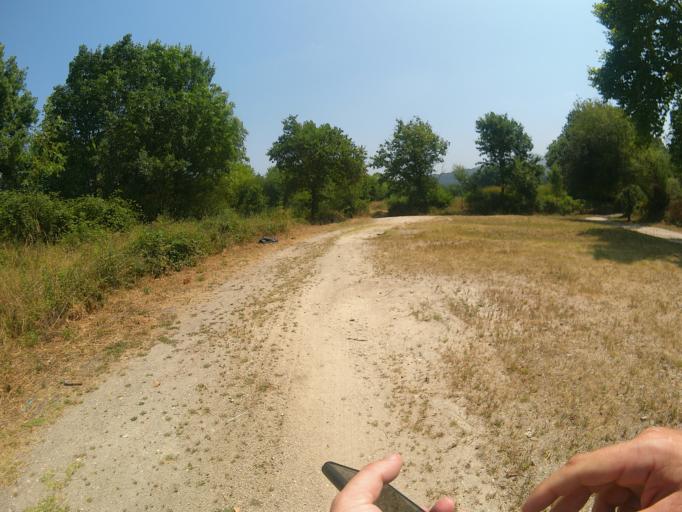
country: PT
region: Viana do Castelo
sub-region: Ponte de Lima
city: Ponte de Lima
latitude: 41.7763
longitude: -8.5710
